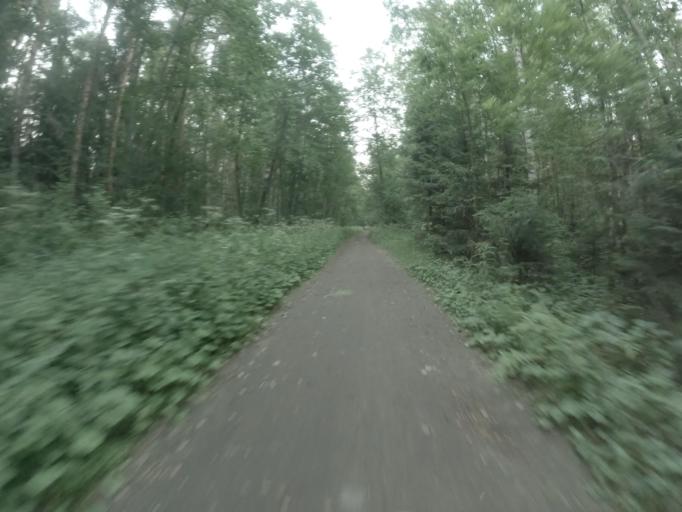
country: RU
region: St.-Petersburg
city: Krasnogvargeisky
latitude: 59.9624
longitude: 30.5459
